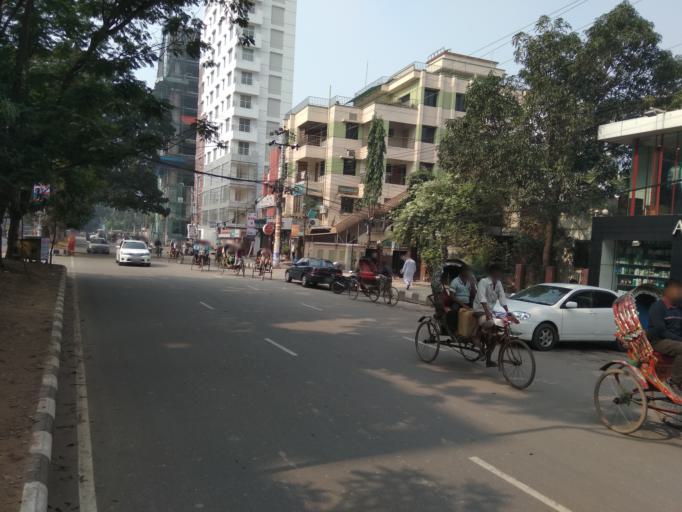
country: BD
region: Dhaka
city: Tungi
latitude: 23.8675
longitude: 90.3954
